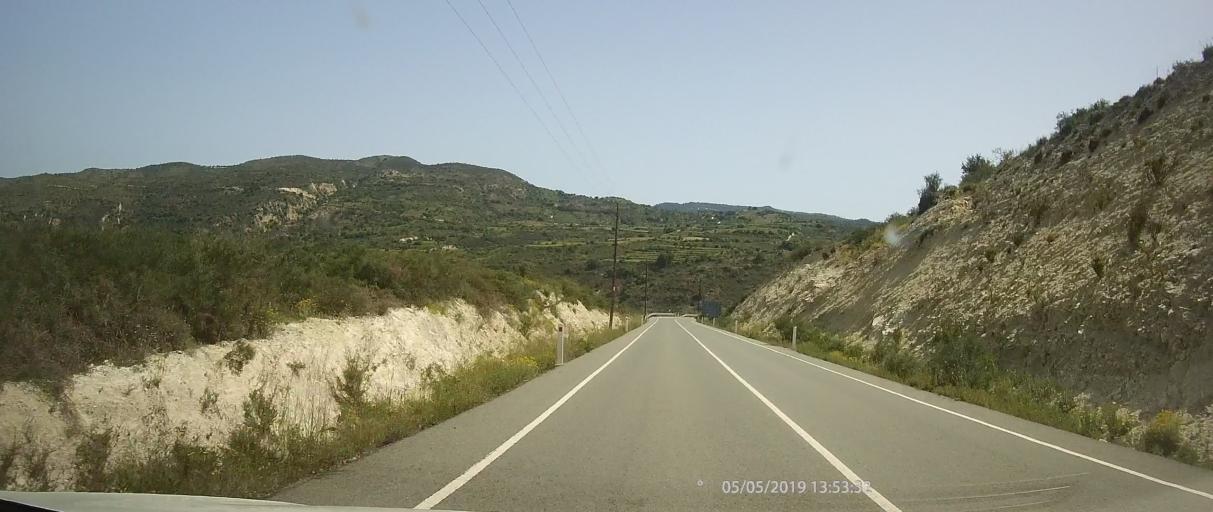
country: CY
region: Limassol
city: Pachna
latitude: 34.8192
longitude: 32.7250
